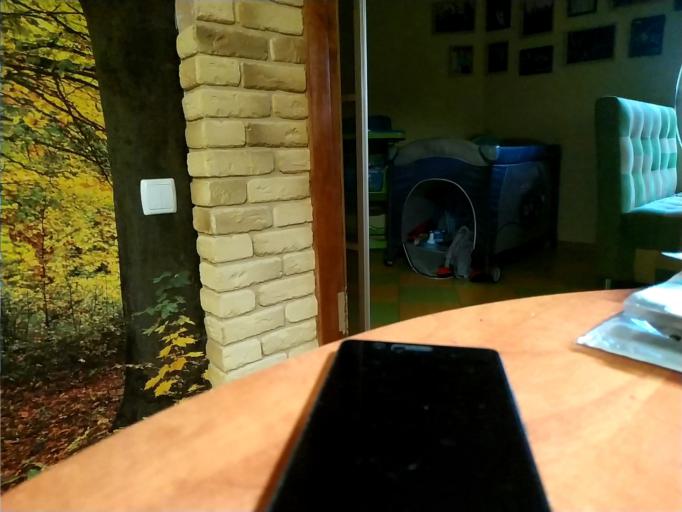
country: RU
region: Orjol
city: Znamenskoye
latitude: 53.4725
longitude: 35.5178
